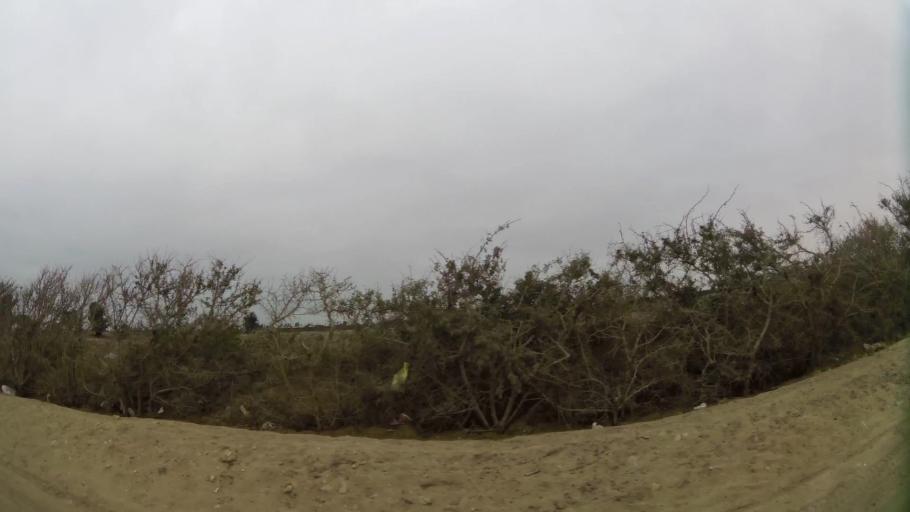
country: PE
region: Ica
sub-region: Provincia de Pisco
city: Villa Tupac Amaru
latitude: -13.7580
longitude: -76.1743
